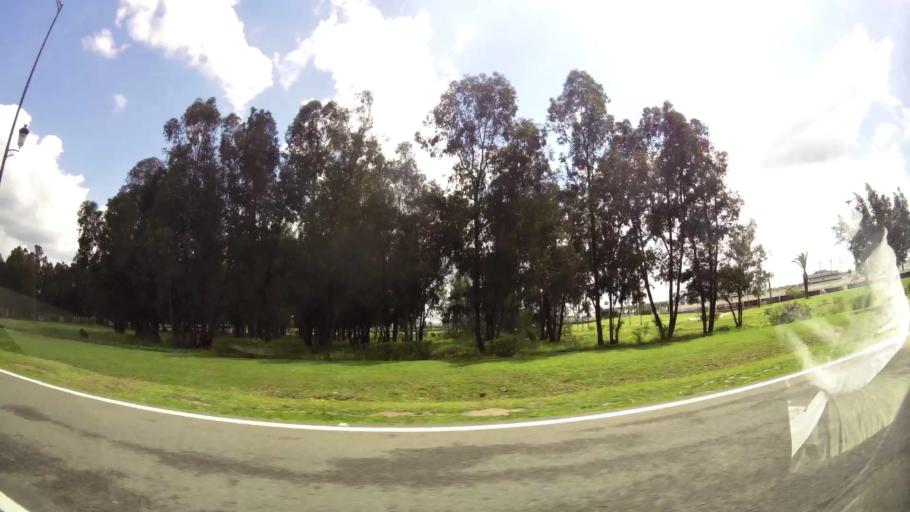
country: MA
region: Chaouia-Ouardigha
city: Nouaseur
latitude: 33.3765
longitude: -7.5774
